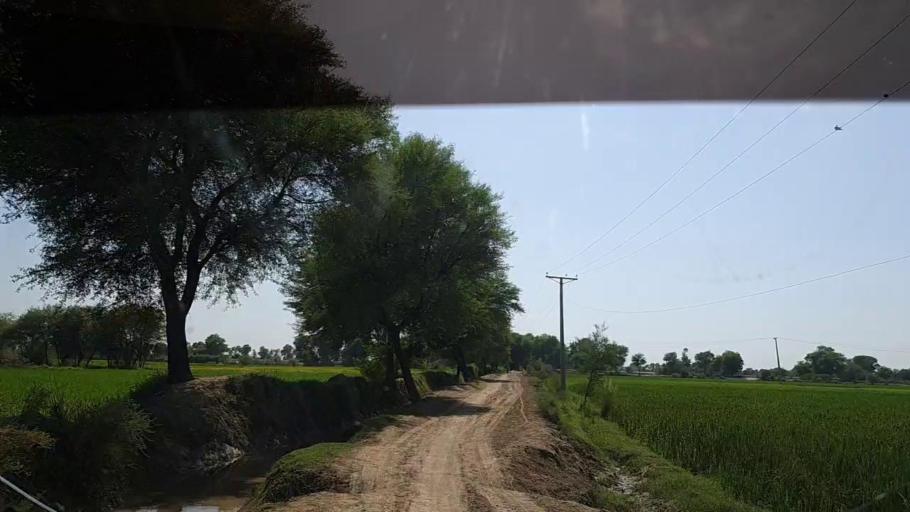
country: PK
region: Sindh
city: Ghauspur
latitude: 28.2208
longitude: 69.0988
